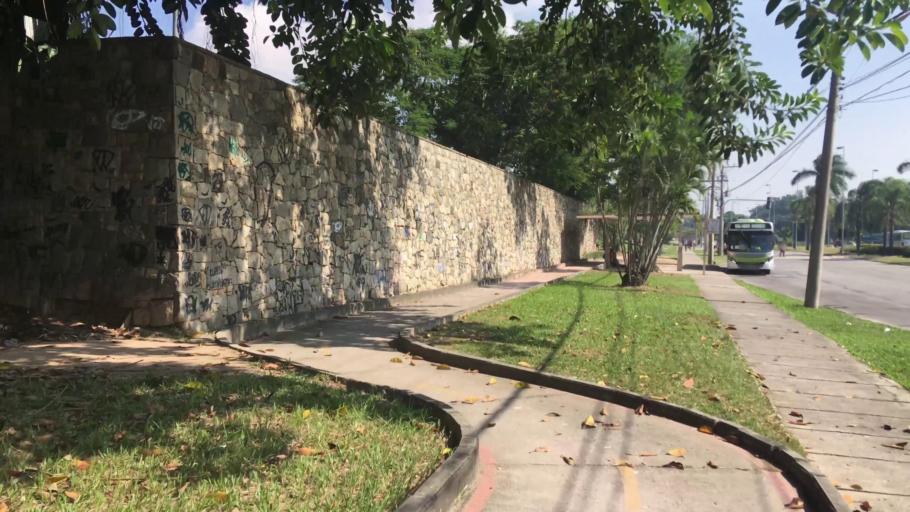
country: BR
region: Rio de Janeiro
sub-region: Rio De Janeiro
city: Rio de Janeiro
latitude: -22.8426
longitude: -43.2327
